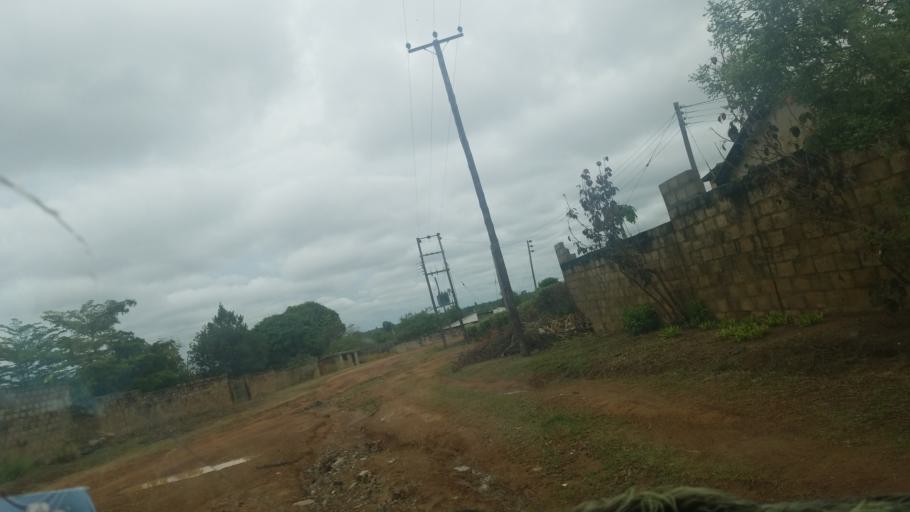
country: ZM
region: Luapula
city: Mansa
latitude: -11.1963
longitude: 28.8982
